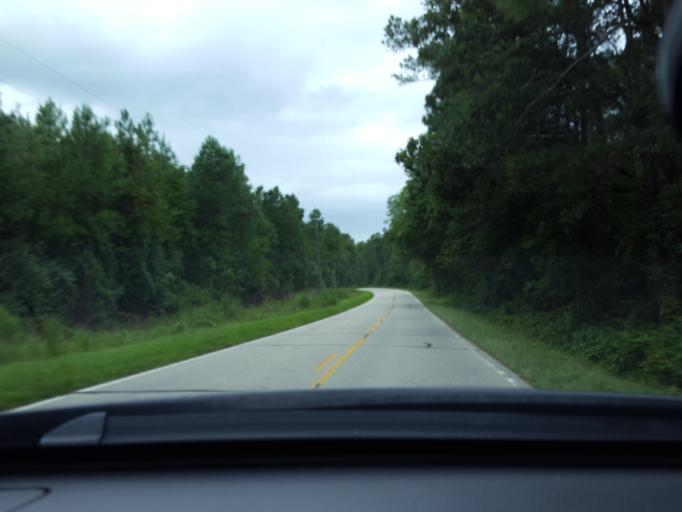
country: US
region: North Carolina
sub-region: Sampson County
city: Clinton
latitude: 34.7982
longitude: -78.2794
